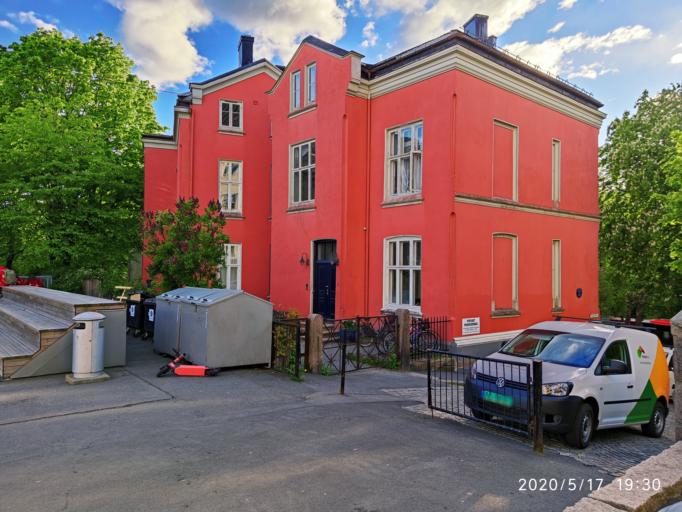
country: NO
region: Oslo
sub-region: Oslo
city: Oslo
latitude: 59.9231
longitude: 10.7280
